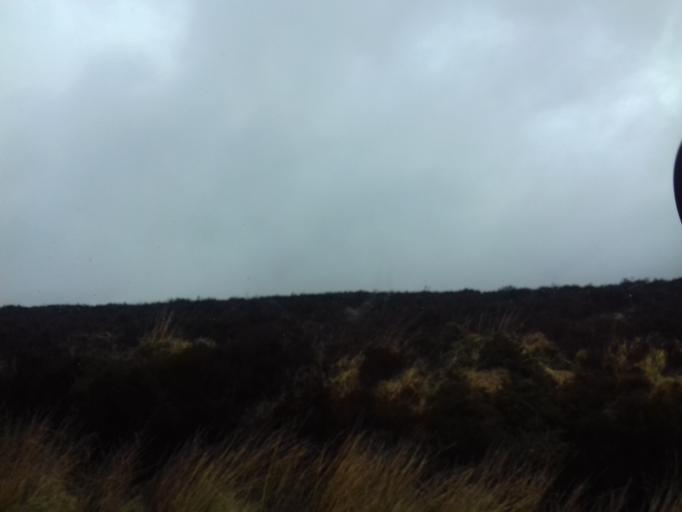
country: IE
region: Leinster
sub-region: Wicklow
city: Enniskerry
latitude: 53.1297
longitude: -6.2945
